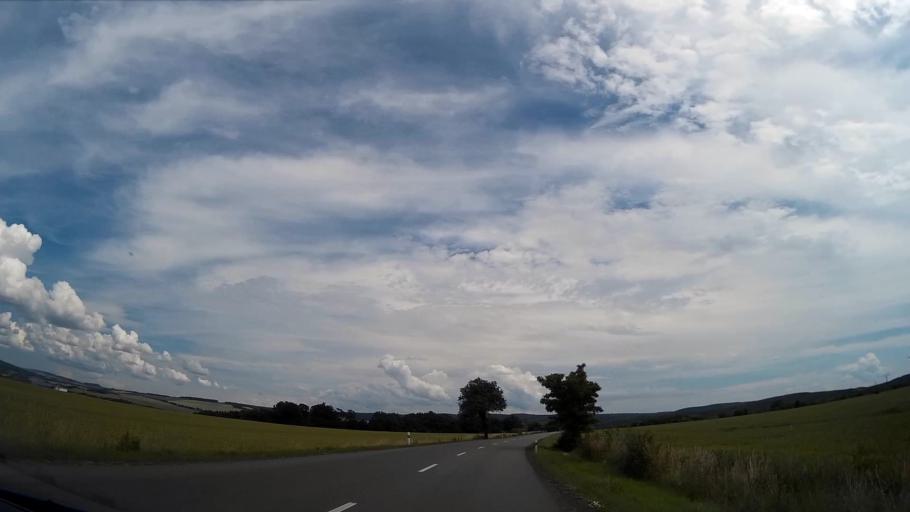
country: CZ
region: South Moravian
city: Ivancice
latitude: 49.0847
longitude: 16.3561
